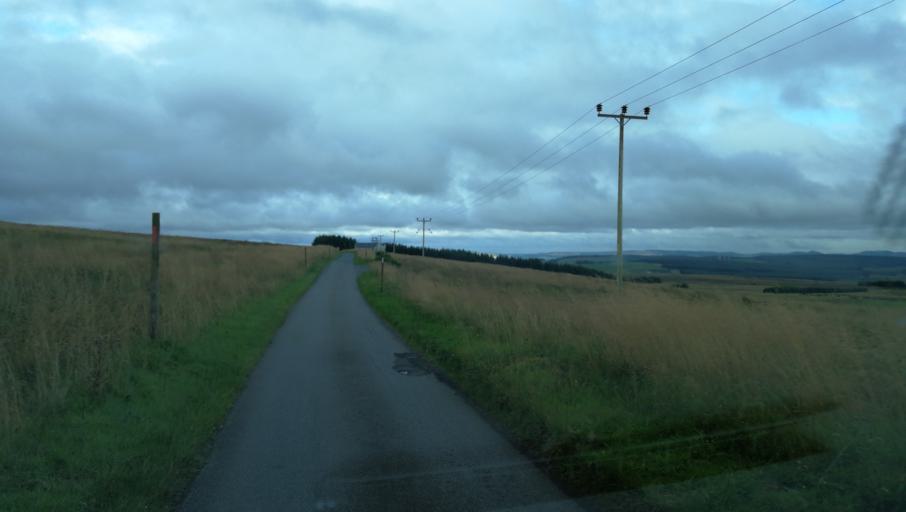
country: GB
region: Scotland
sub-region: Perth and Kinross
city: Blairgowrie
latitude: 56.6733
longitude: -3.3542
